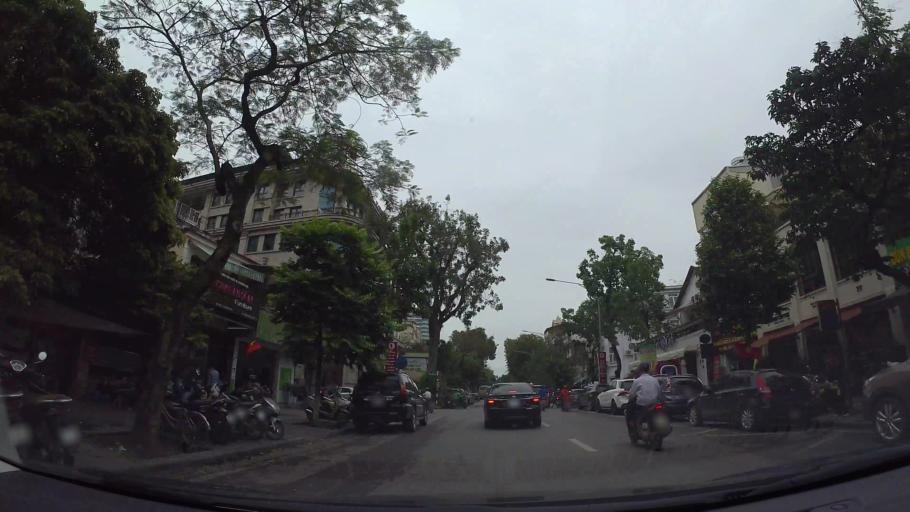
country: VN
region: Ha Noi
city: Hai BaTrung
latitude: 21.0207
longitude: 105.8482
